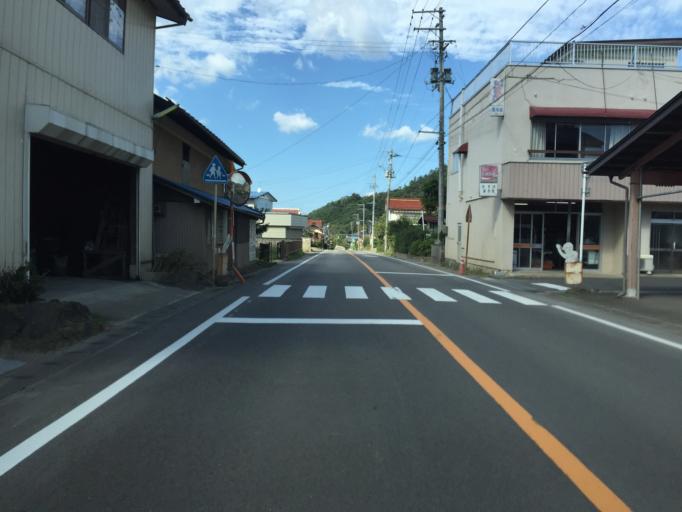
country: JP
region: Fukushima
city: Yanagawamachi-saiwaicho
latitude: 37.8147
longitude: 140.6195
